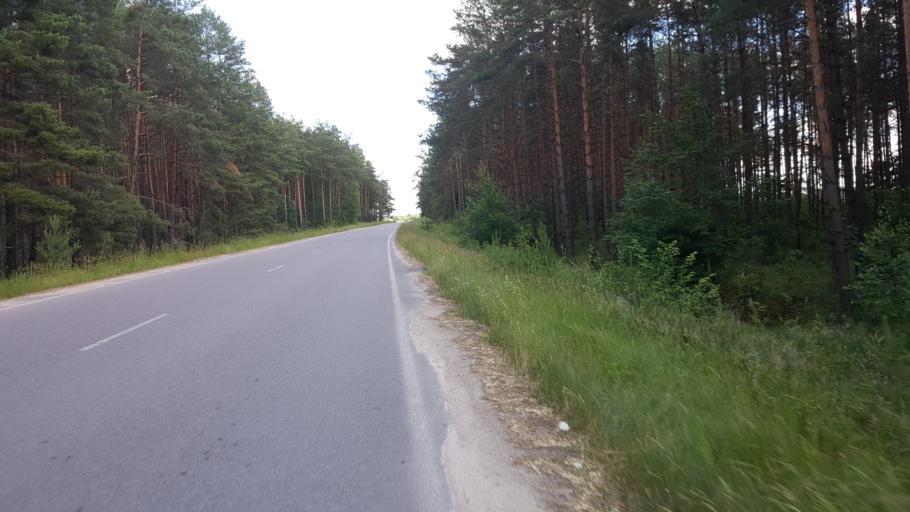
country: PL
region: Podlasie
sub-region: Powiat hajnowski
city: Czeremcha
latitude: 52.5404
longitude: 23.5212
